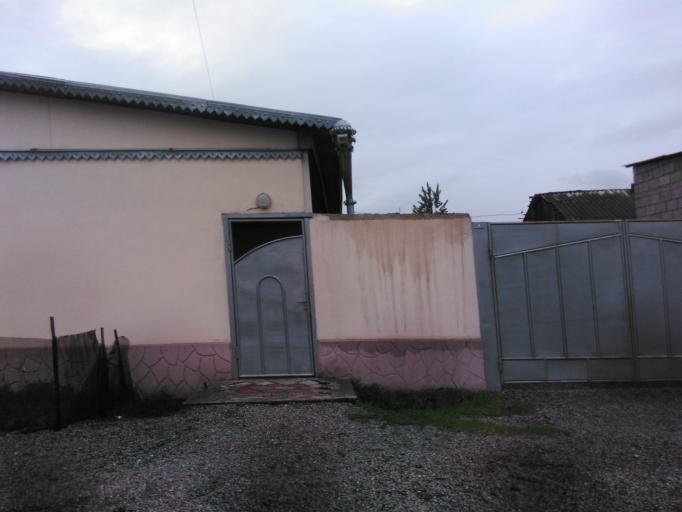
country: KG
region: Chuy
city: Tokmok
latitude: 42.8150
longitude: 75.3224
